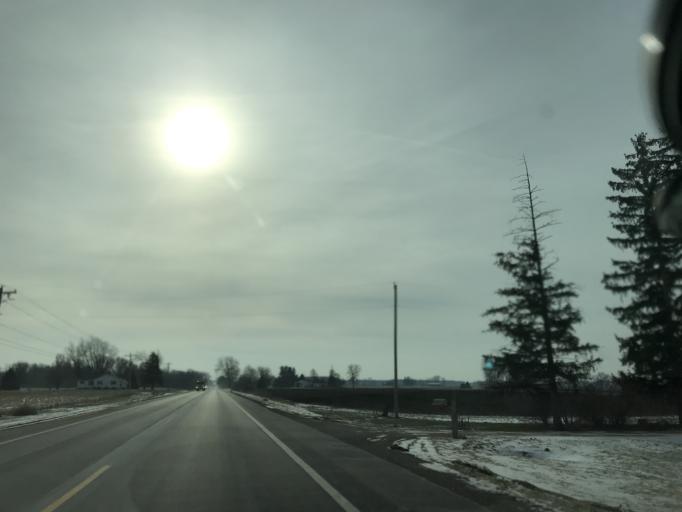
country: US
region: Michigan
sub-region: Ionia County
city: Lake Odessa
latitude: 42.8623
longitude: -85.0750
